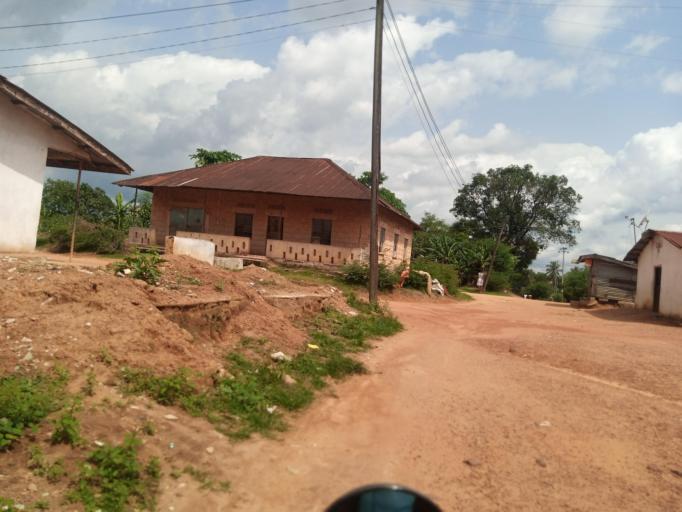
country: SL
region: Southern Province
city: Bo
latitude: 7.9766
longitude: -11.7343
